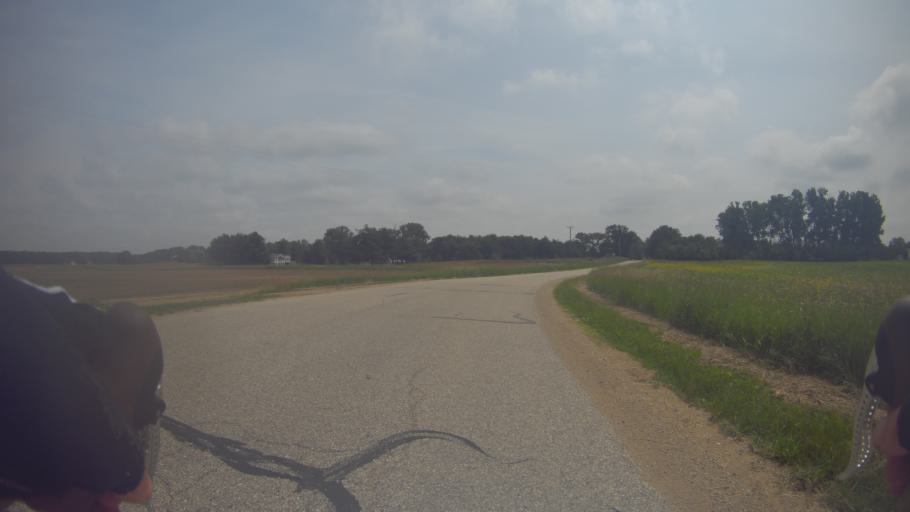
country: US
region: Wisconsin
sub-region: Jefferson County
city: Cambridge
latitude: 42.9680
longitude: -89.0082
